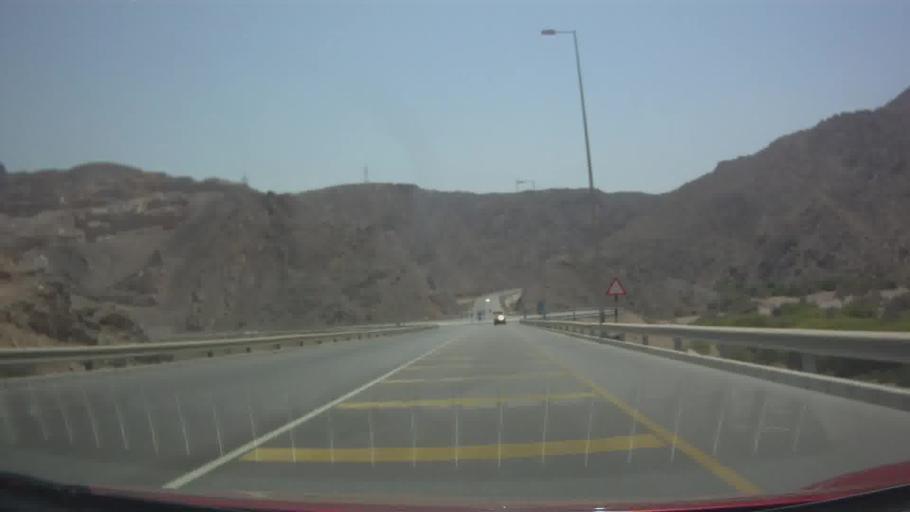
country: OM
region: Muhafazat Masqat
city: Muscat
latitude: 23.5361
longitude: 58.6494
